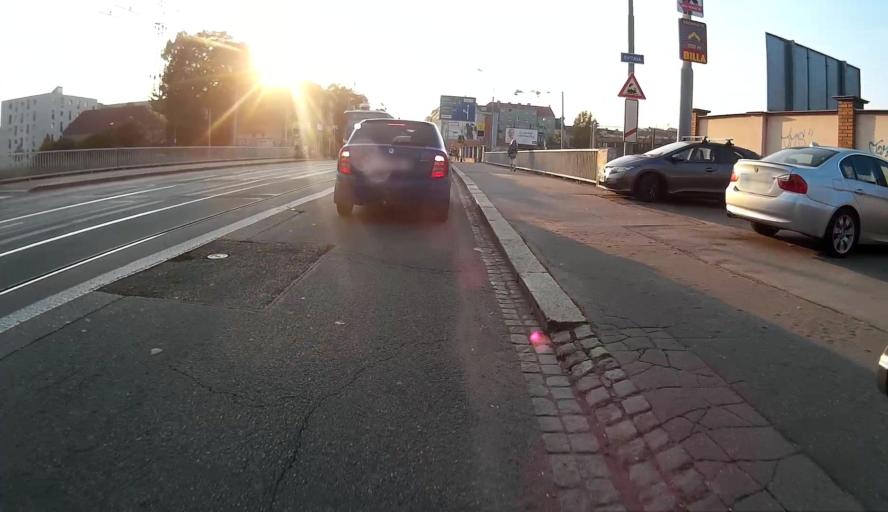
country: CZ
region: South Moravian
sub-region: Mesto Brno
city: Brno
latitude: 49.1913
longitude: 16.6291
